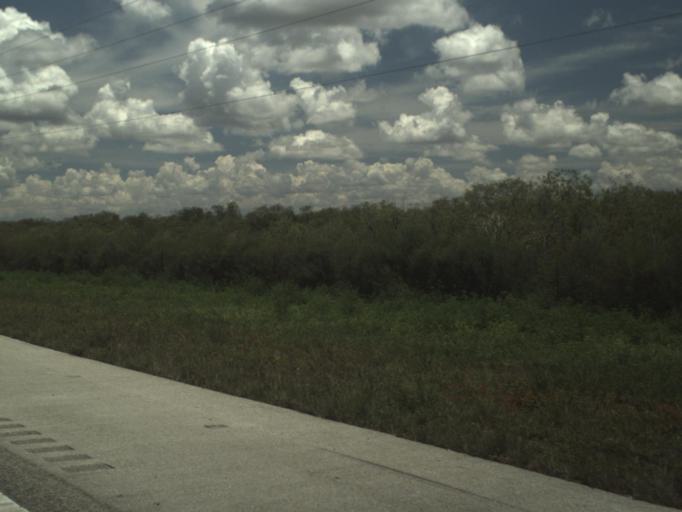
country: US
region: Florida
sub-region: Broward County
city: Weston
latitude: 26.1521
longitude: -80.7372
